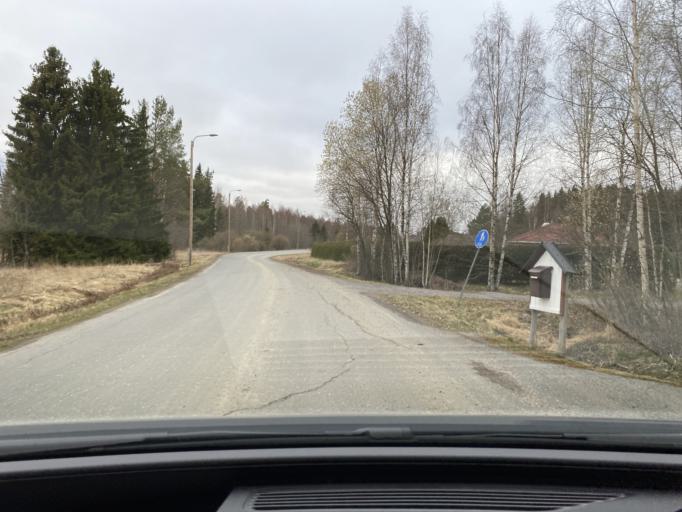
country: FI
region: Satakunta
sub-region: Pori
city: Huittinen
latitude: 61.1637
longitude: 22.7290
